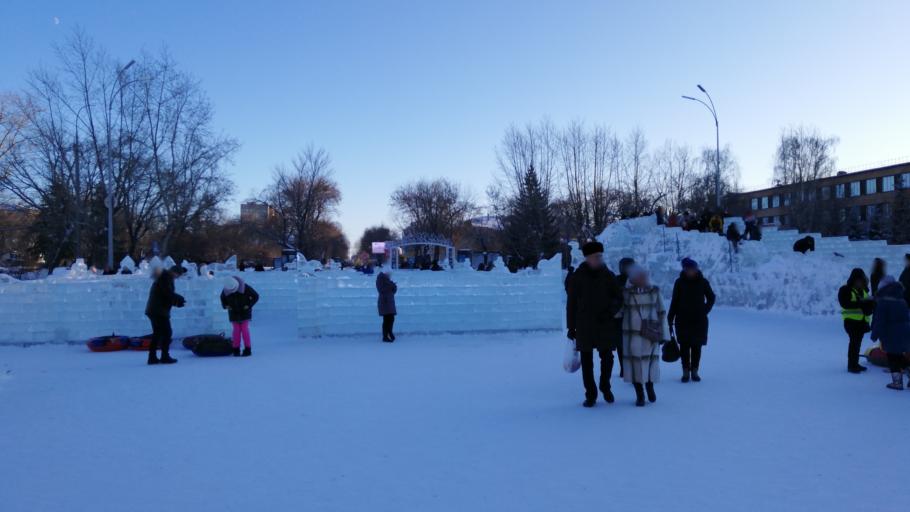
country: KZ
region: Soltustik Qazaqstan
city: Petropavlovsk
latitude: 54.8668
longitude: 69.1338
